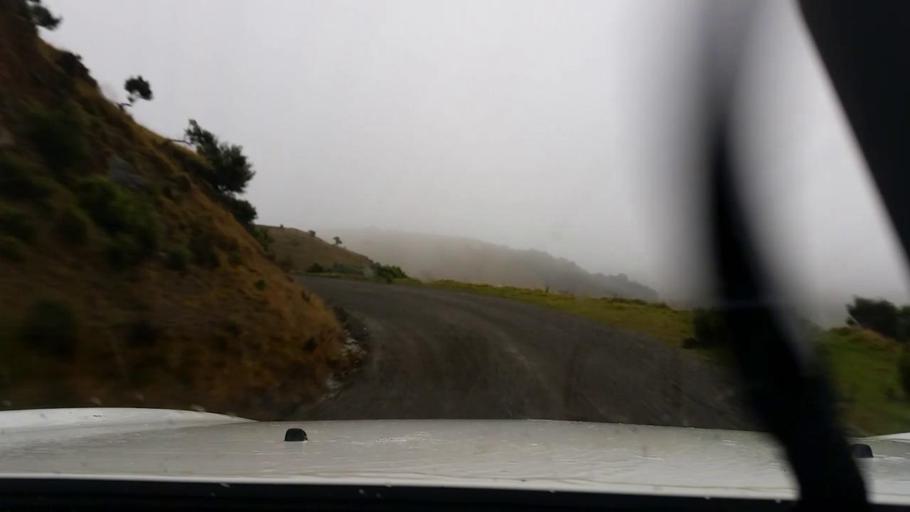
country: NZ
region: Wellington
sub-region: Masterton District
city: Masterton
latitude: -41.2491
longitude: 175.8836
